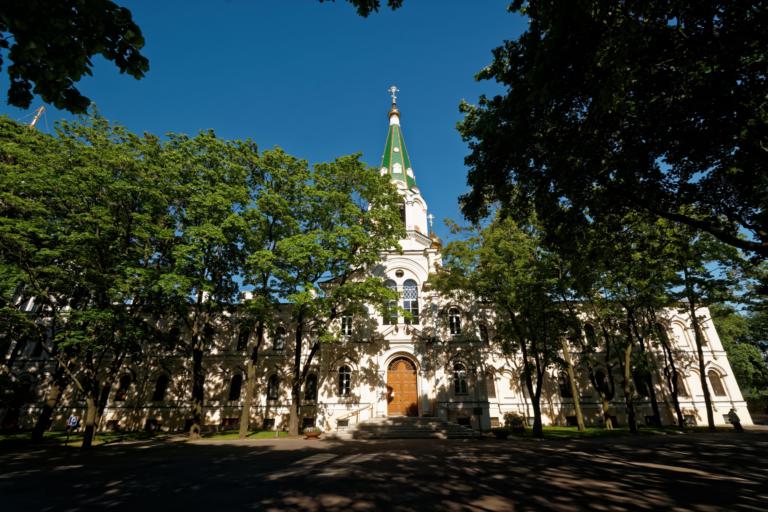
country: RU
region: St.-Petersburg
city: Admiralteisky
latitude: 59.8980
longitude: 30.3199
